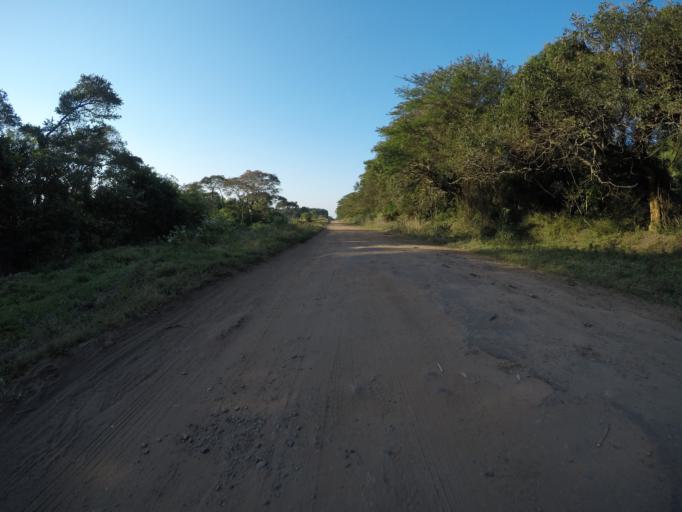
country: ZA
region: KwaZulu-Natal
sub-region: uThungulu District Municipality
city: KwaMbonambi
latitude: -28.7018
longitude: 32.1909
